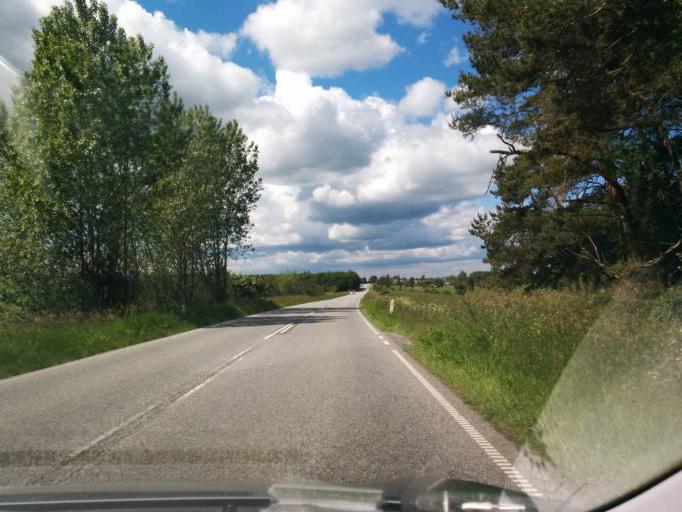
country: DK
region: Central Jutland
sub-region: Syddjurs Kommune
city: Ebeltoft
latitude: 56.2780
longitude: 10.5946
